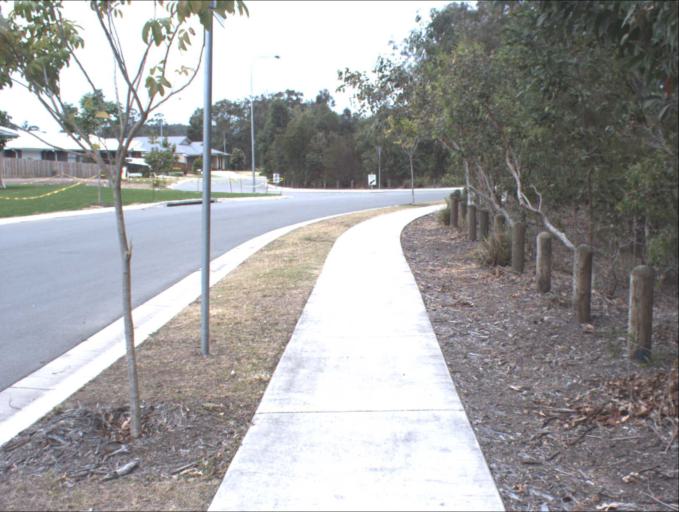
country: AU
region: Queensland
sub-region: Logan
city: Beenleigh
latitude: -27.6603
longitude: 153.2036
